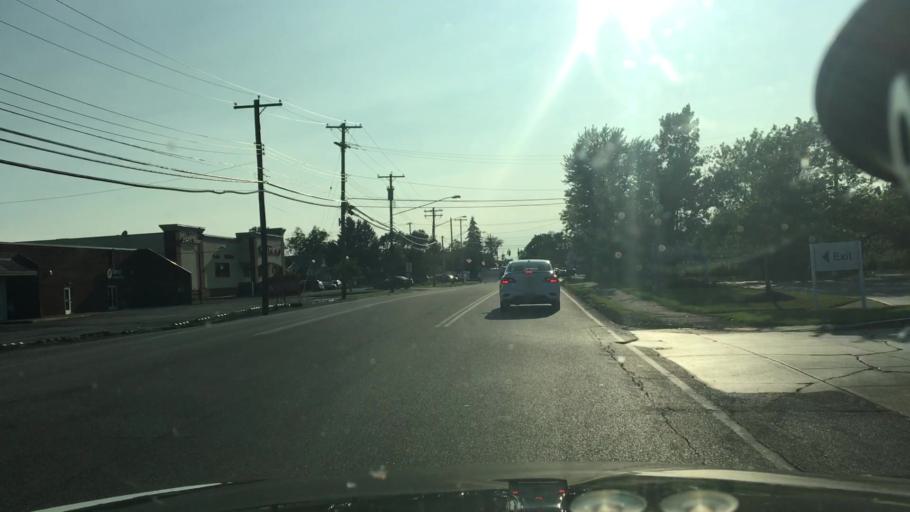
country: US
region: New York
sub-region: Erie County
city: Blasdell
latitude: 42.7972
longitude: -78.8217
